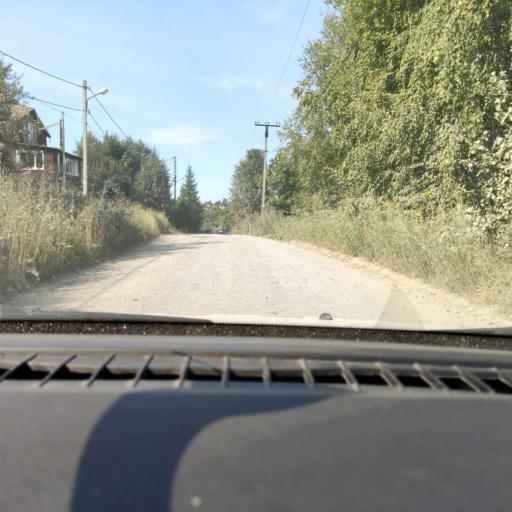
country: RU
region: Perm
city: Polazna
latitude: 58.1391
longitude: 56.4574
